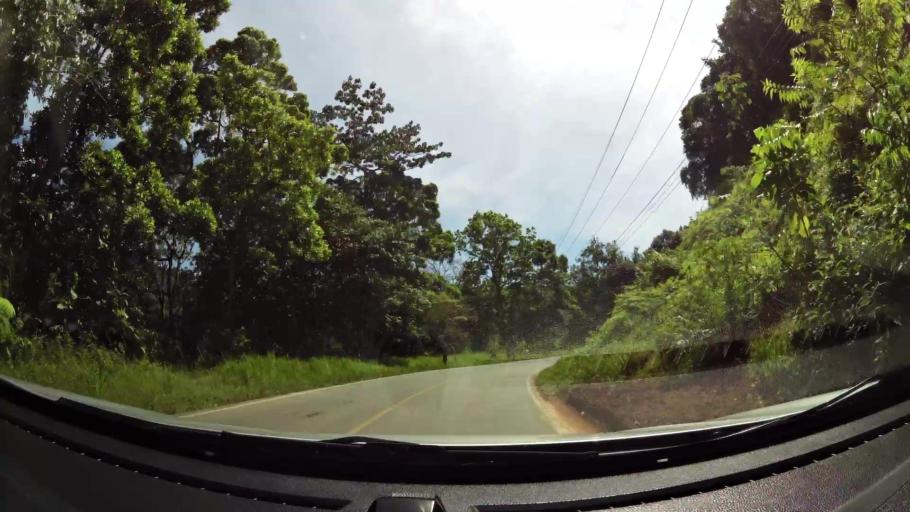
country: CR
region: San Jose
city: San Isidro
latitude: 9.2638
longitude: -83.8625
